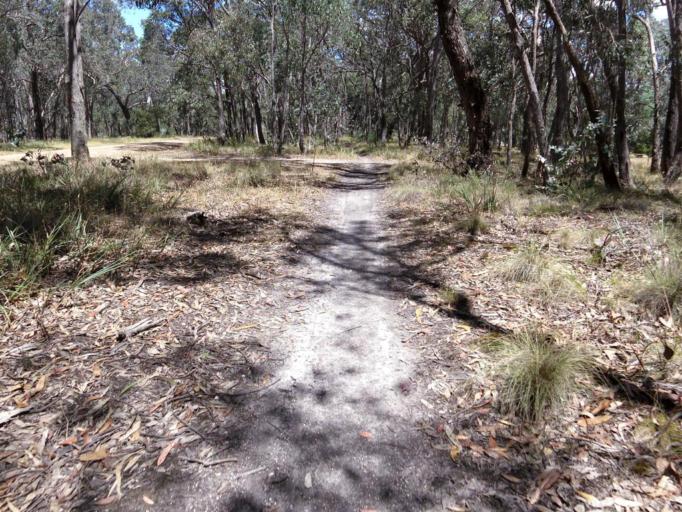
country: AU
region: Victoria
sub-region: Melton
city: Melton West
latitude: -37.4943
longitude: 144.5474
